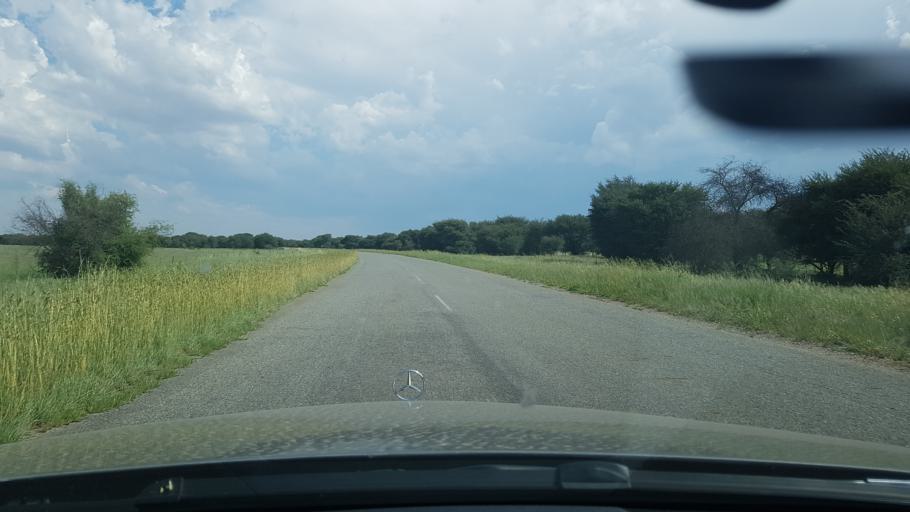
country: ZA
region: North-West
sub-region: Dr Ruth Segomotsi Mompati District Municipality
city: Bloemhof
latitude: -27.7198
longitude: 25.5787
